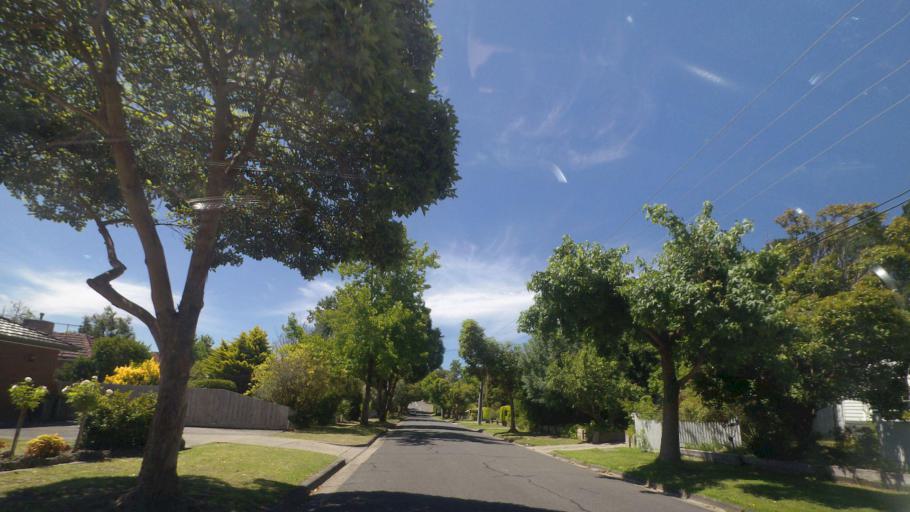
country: AU
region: Victoria
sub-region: Maroondah
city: Ringwood East
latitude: -37.8017
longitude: 145.2308
